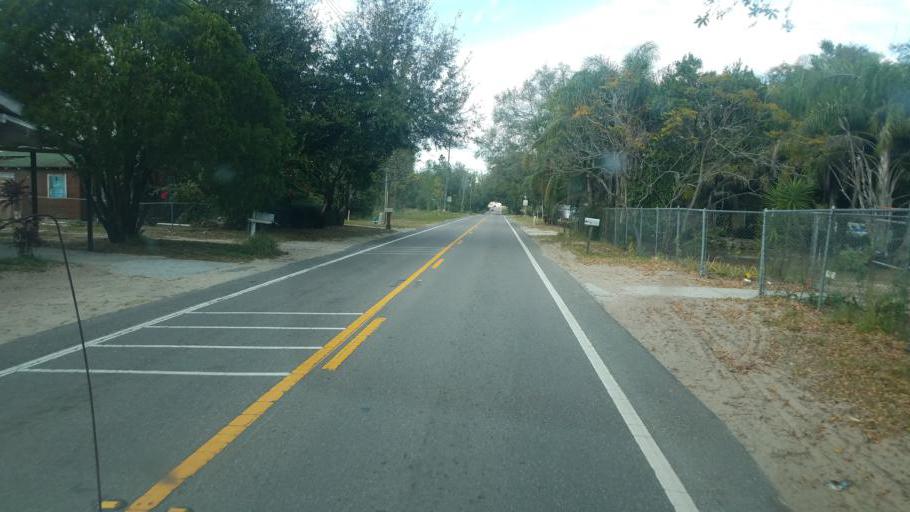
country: US
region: Florida
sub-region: Polk County
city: Haines City
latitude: 28.1090
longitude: -81.6068
